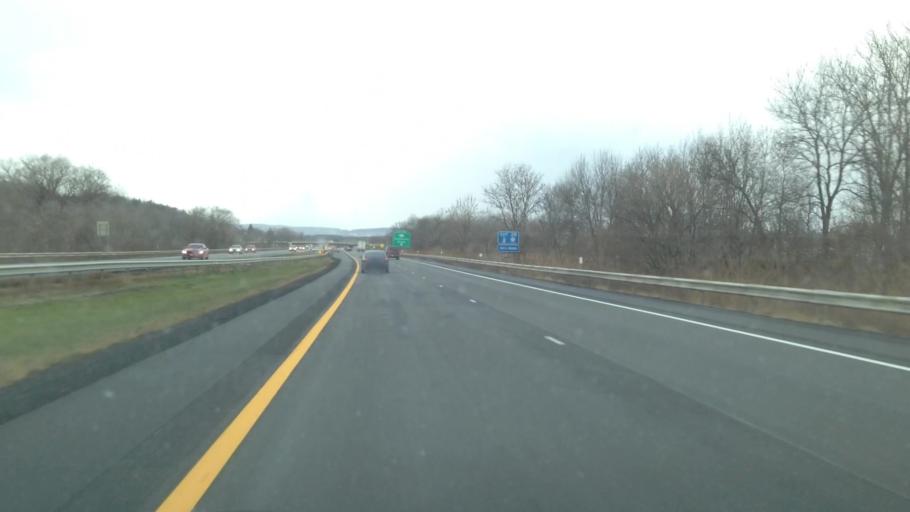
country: US
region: New York
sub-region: Montgomery County
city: Fonda
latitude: 42.9429
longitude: -74.3497
